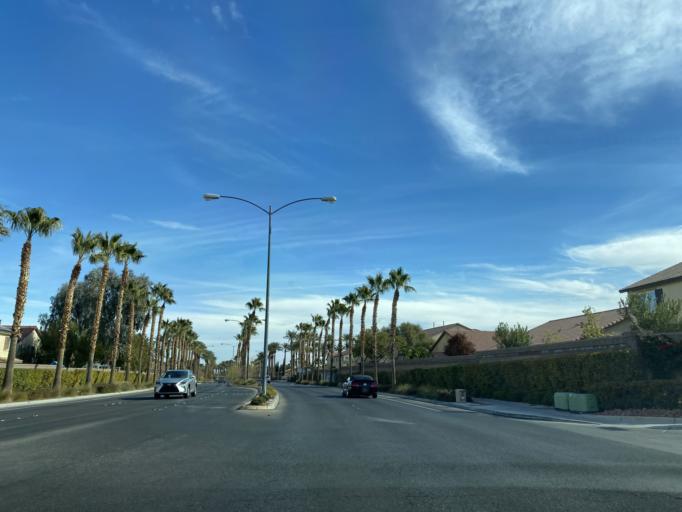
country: US
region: Nevada
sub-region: Clark County
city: Enterprise
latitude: 36.0480
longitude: -115.2534
